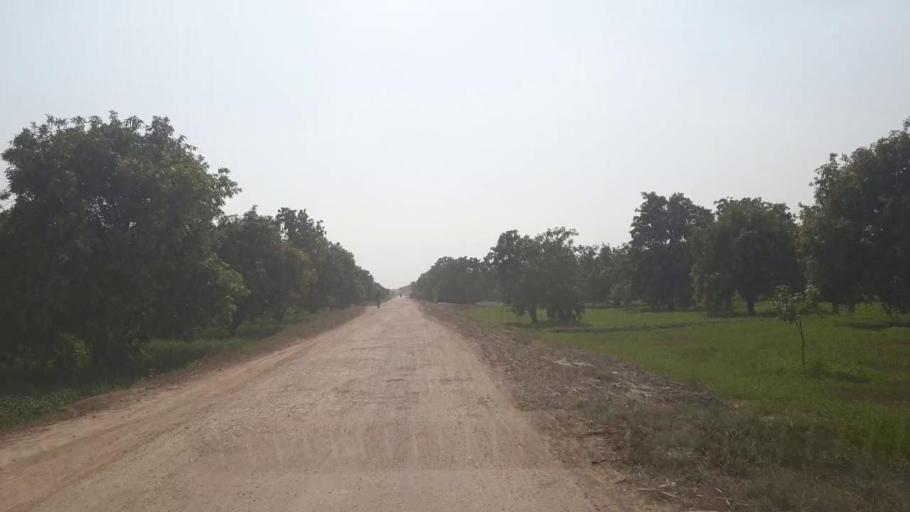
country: PK
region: Sindh
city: Tando Allahyar
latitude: 25.4823
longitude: 68.8350
